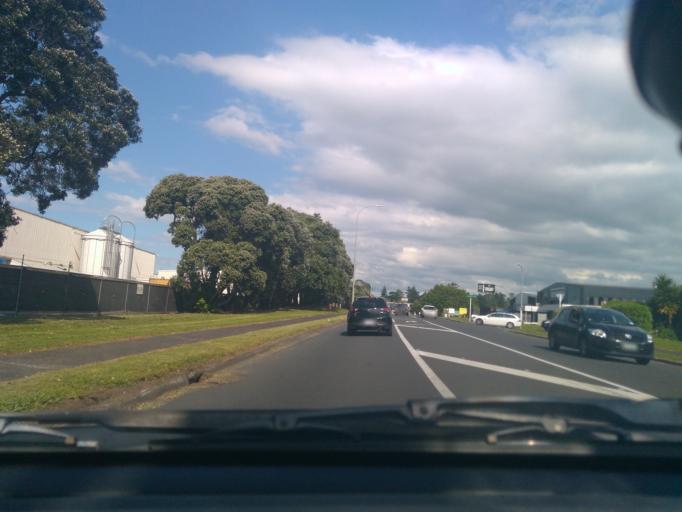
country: NZ
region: Auckland
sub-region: Auckland
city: Manukau City
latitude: -36.9472
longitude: 174.8881
